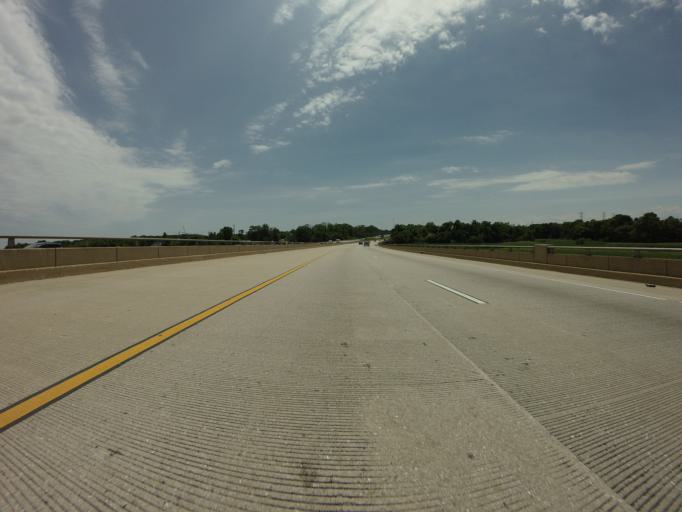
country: US
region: Maryland
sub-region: Baltimore County
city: Rosedale
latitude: 39.3050
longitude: -76.5008
